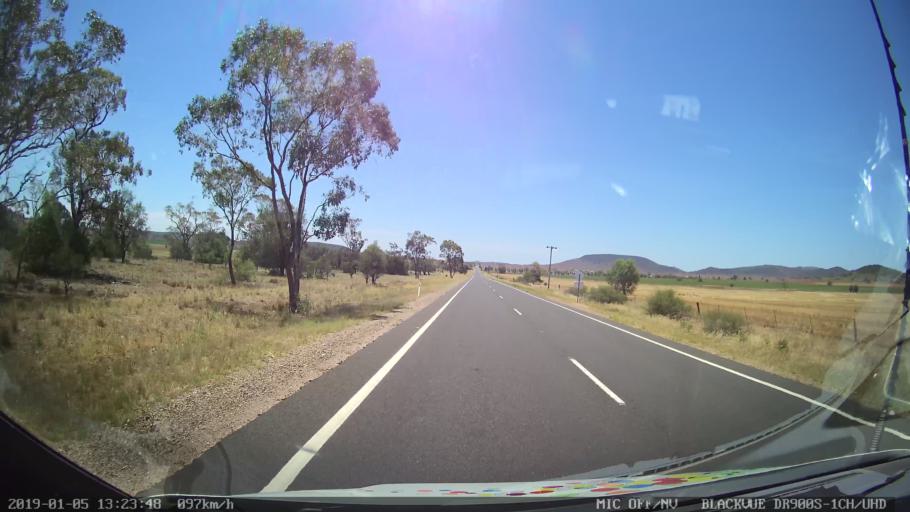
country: AU
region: New South Wales
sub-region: Gunnedah
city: Gunnedah
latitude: -31.0750
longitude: 149.9800
